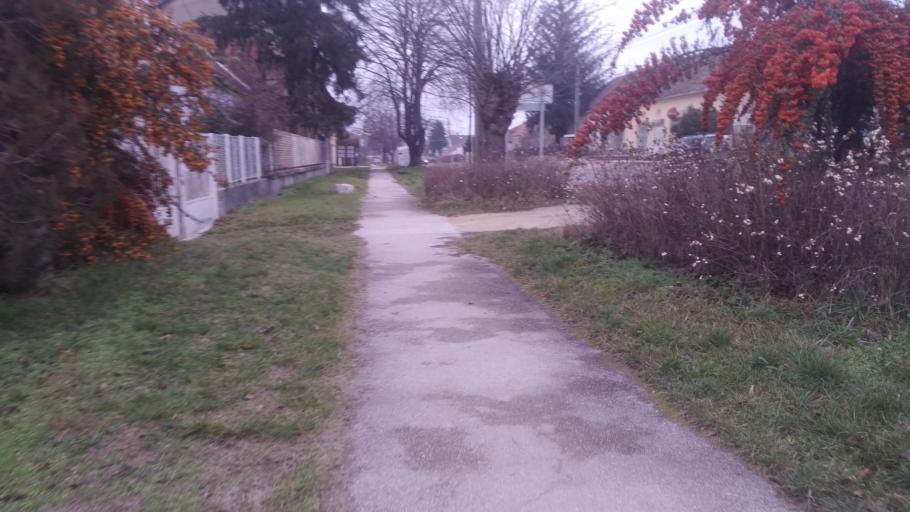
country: HU
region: Komarom-Esztergom
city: Dunaalmas
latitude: 47.7338
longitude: 18.3313
